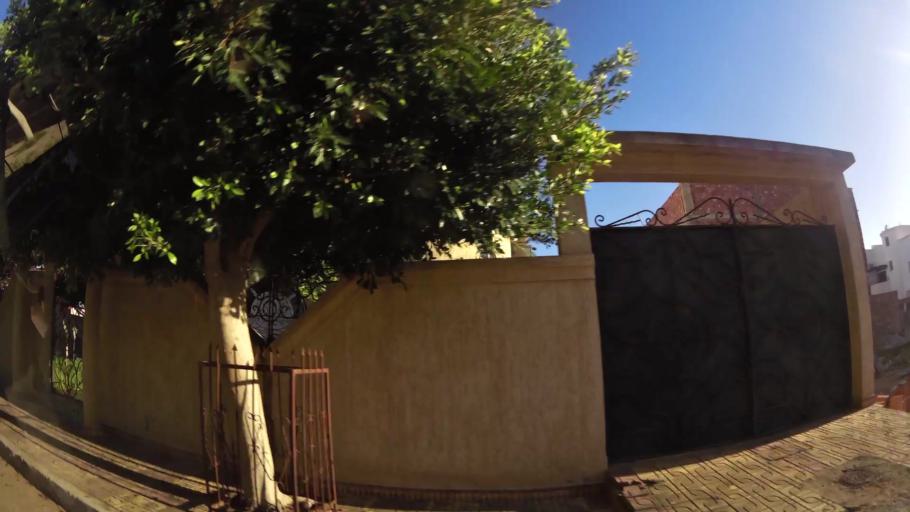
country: MA
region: Oriental
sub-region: Berkane-Taourirt
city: Madagh
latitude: 35.0880
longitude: -2.2463
